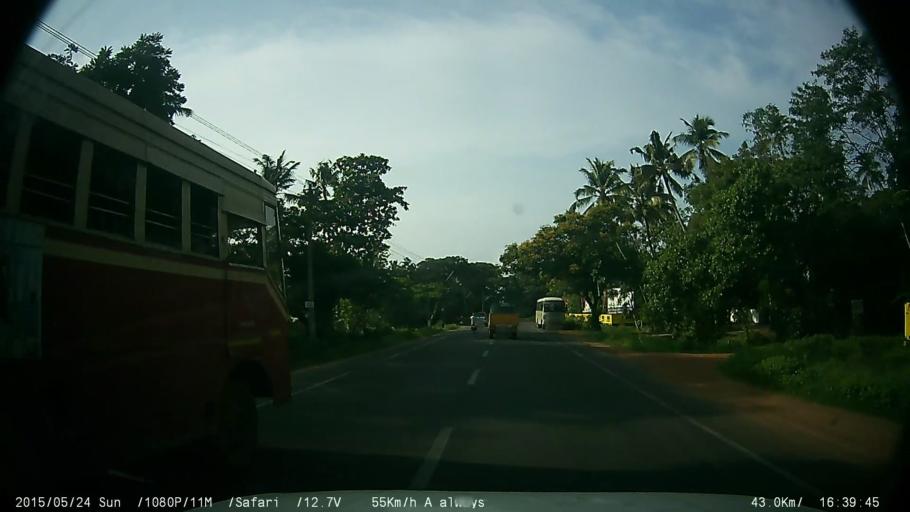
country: IN
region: Kerala
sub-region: Alappuzha
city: Shertallai
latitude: 9.6179
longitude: 76.3311
